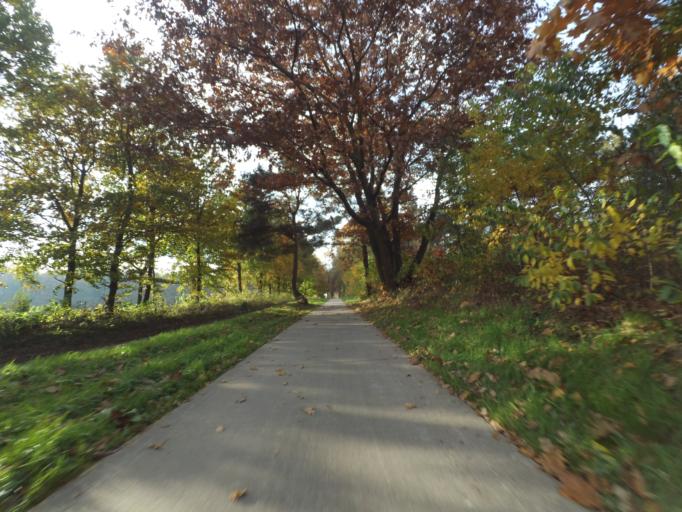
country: NL
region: Gelderland
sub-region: Gemeente Renkum
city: Renkum
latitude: 52.0168
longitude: 5.7300
